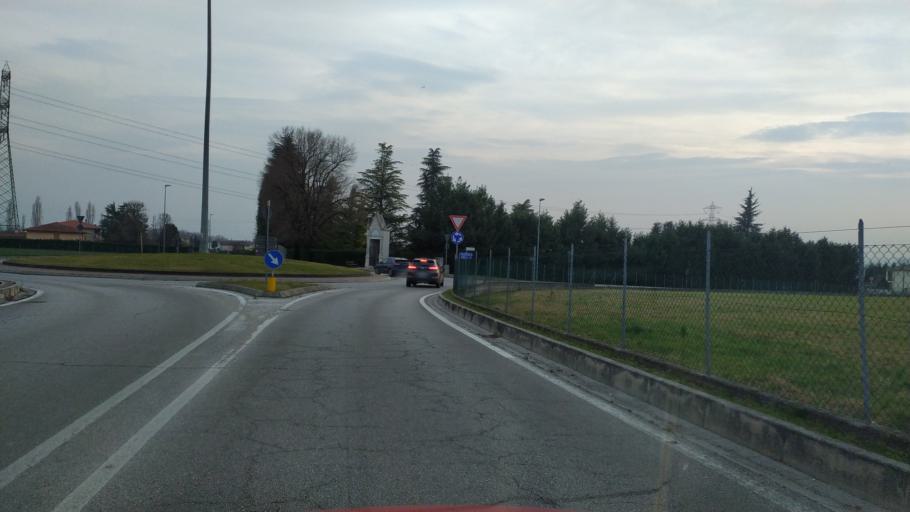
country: IT
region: Veneto
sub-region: Provincia di Vicenza
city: Montecchio Precalcino
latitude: 45.6589
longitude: 11.5581
